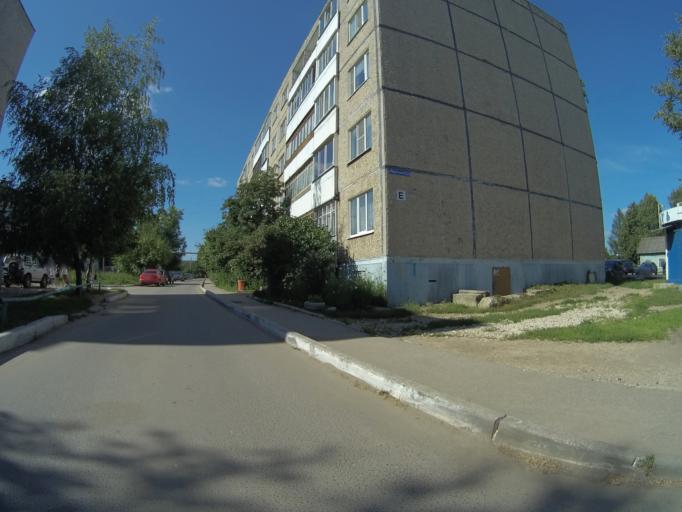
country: RU
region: Vladimir
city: Vorsha
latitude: 56.0980
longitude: 40.2023
